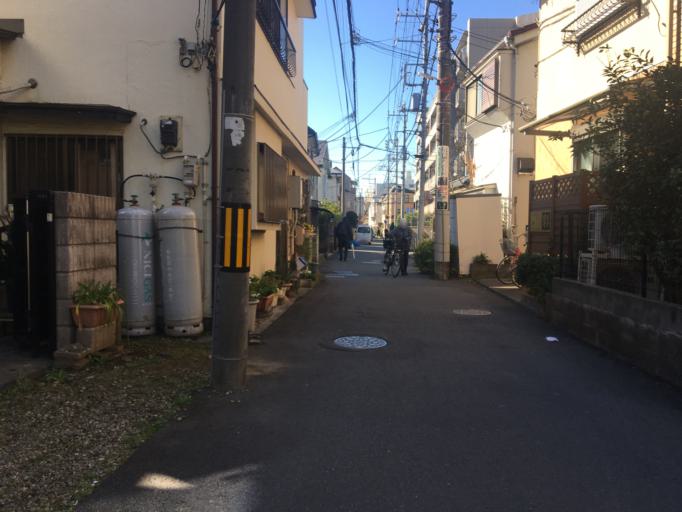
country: JP
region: Saitama
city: Shiki
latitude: 35.8193
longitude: 139.5694
